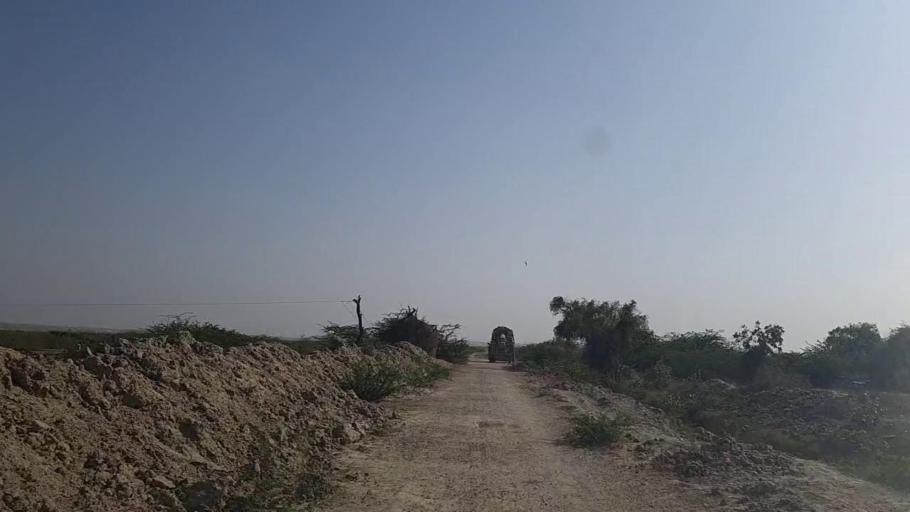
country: PK
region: Sindh
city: Kadhan
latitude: 24.5791
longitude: 69.2628
